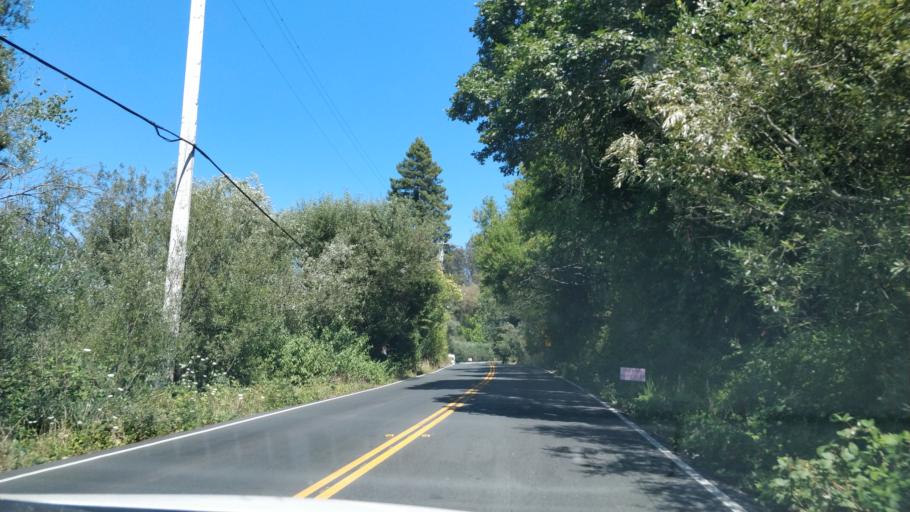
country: US
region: California
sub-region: Sonoma County
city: Graton
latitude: 38.3954
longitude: -122.8692
